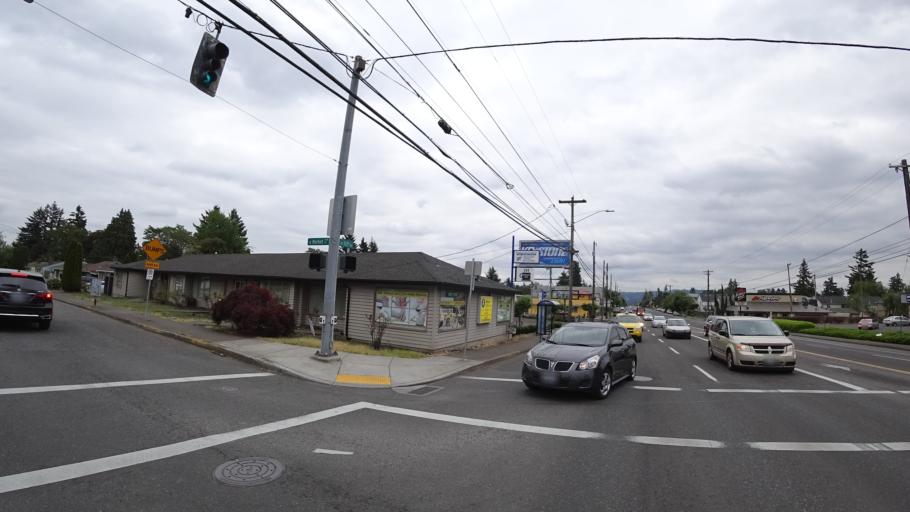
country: US
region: Oregon
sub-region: Multnomah County
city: Lents
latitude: 45.5116
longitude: -122.5376
